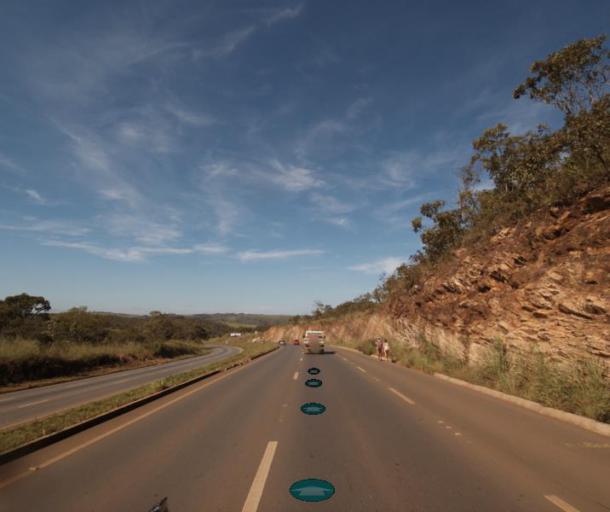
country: BR
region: Federal District
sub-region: Brasilia
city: Brasilia
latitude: -15.7781
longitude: -48.2339
